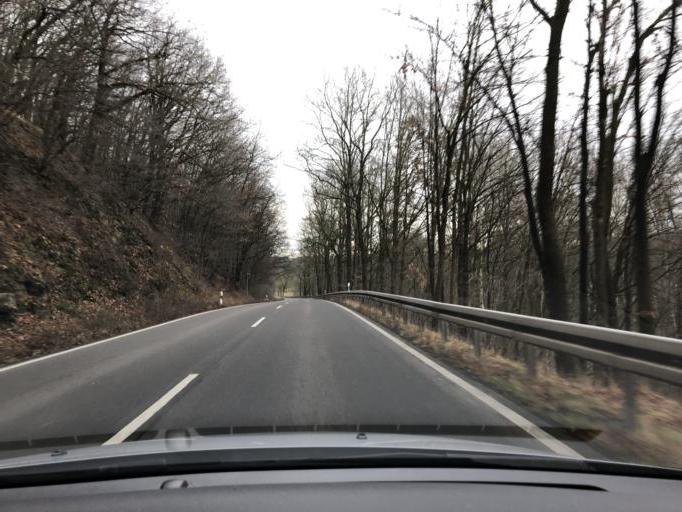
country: DE
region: Saxony
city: Niederstriegis
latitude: 51.0741
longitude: 13.1623
